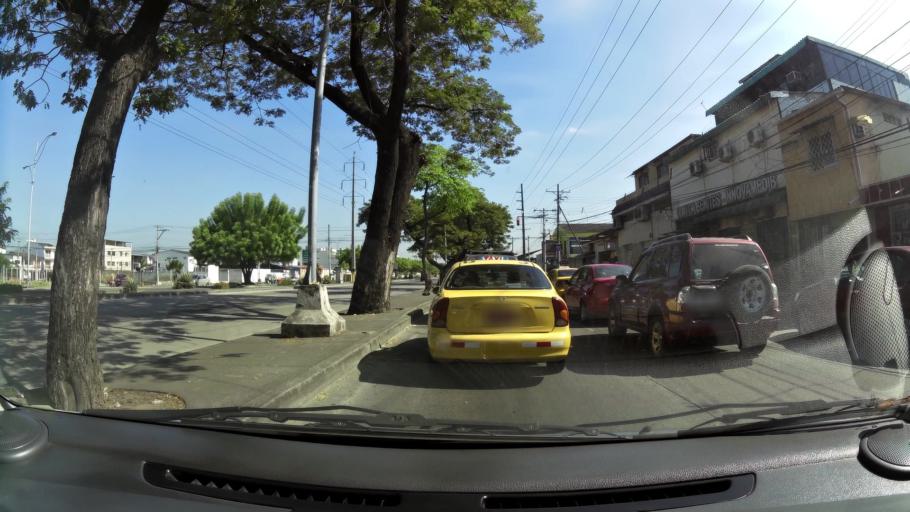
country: EC
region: Guayas
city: Eloy Alfaro
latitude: -2.1430
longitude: -79.9025
